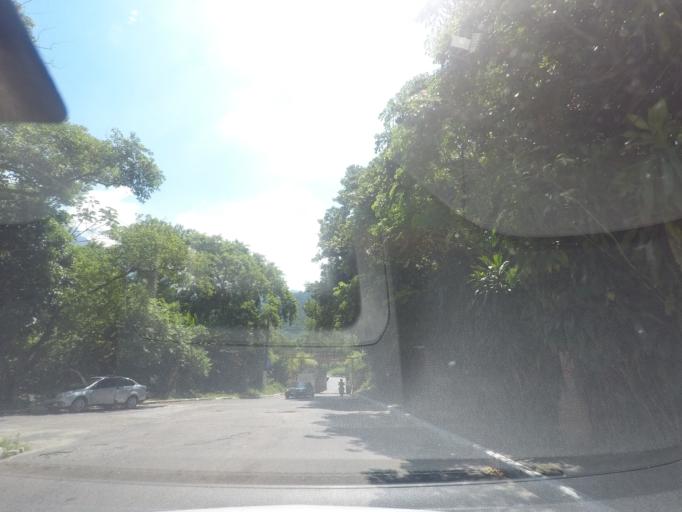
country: BR
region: Rio de Janeiro
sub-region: Petropolis
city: Petropolis
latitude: -22.5762
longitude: -43.1860
